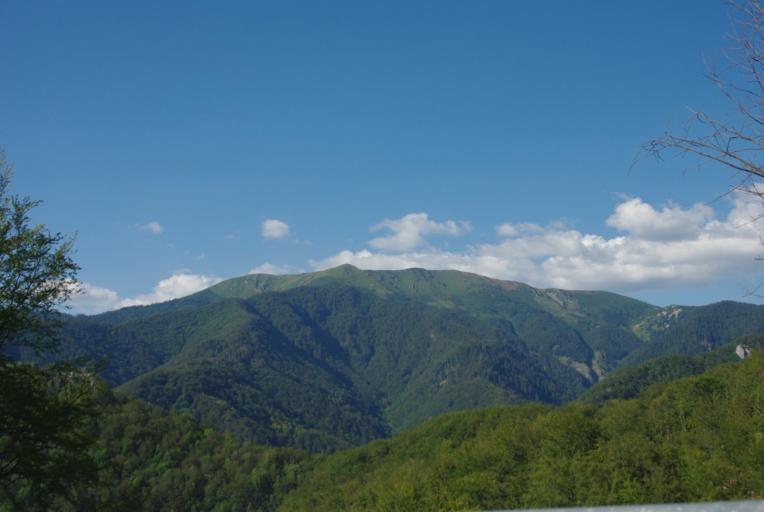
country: RO
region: Bihor
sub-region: Comuna Pietroasa
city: Pietroasa
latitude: 46.5978
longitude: 22.6606
